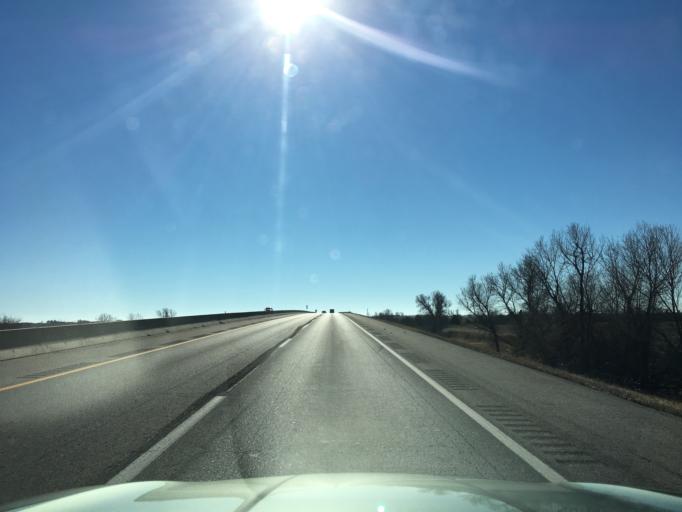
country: US
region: Kansas
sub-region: Sumner County
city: Wellington
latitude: 37.0760
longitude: -97.3386
